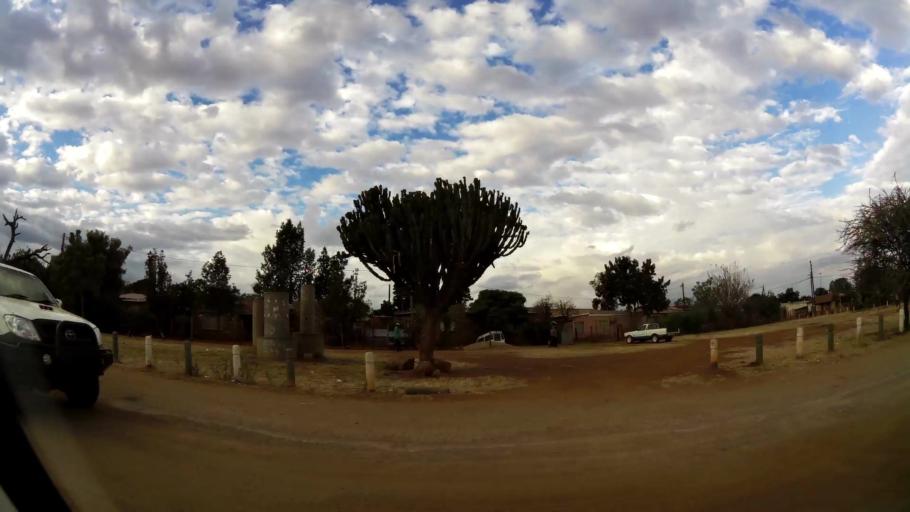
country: ZA
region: Limpopo
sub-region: Waterberg District Municipality
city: Modimolle
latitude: -24.5205
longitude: 28.7221
